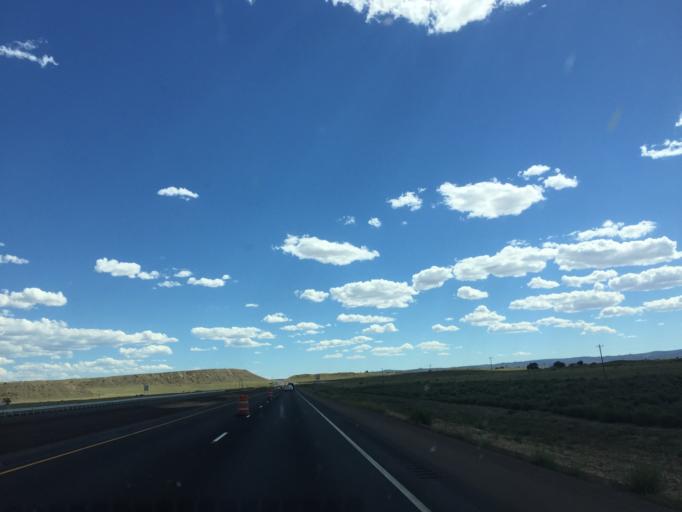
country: US
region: New Mexico
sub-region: McKinley County
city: Twin Lakes
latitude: 35.8220
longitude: -108.7635
